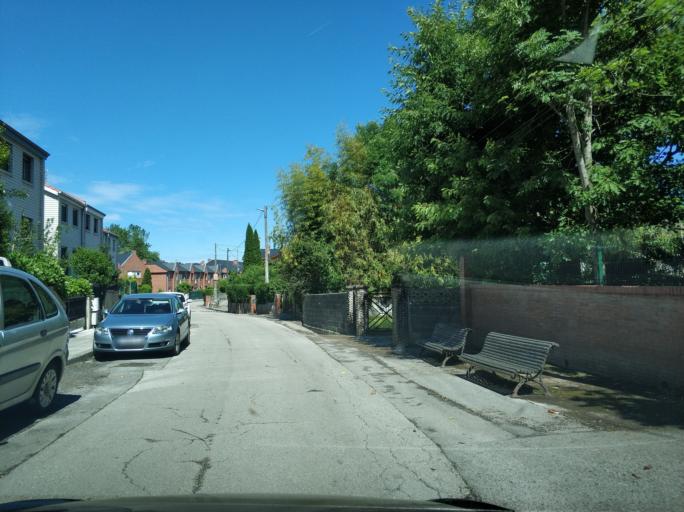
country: ES
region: Cantabria
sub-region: Provincia de Cantabria
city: Puente Viesgo
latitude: 43.3531
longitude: -3.9465
